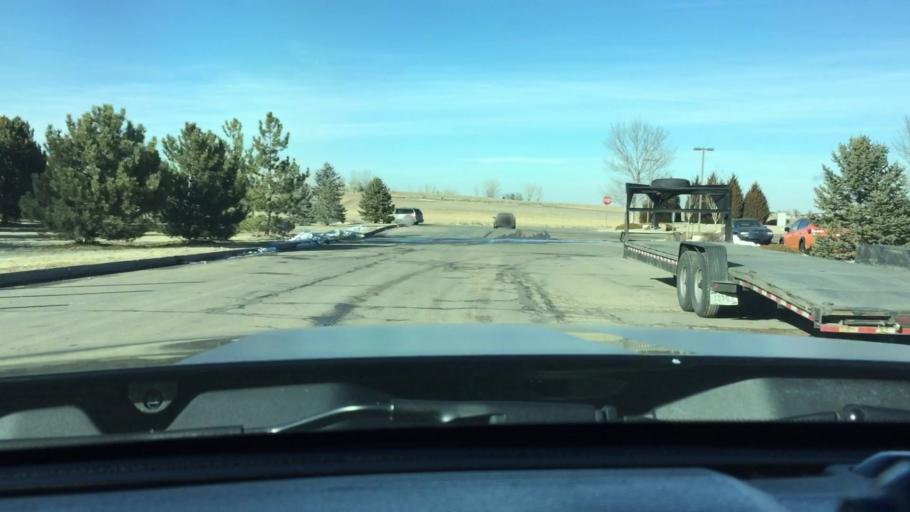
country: US
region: Colorado
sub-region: Weld County
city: Johnstown
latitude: 40.3628
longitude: -104.9771
